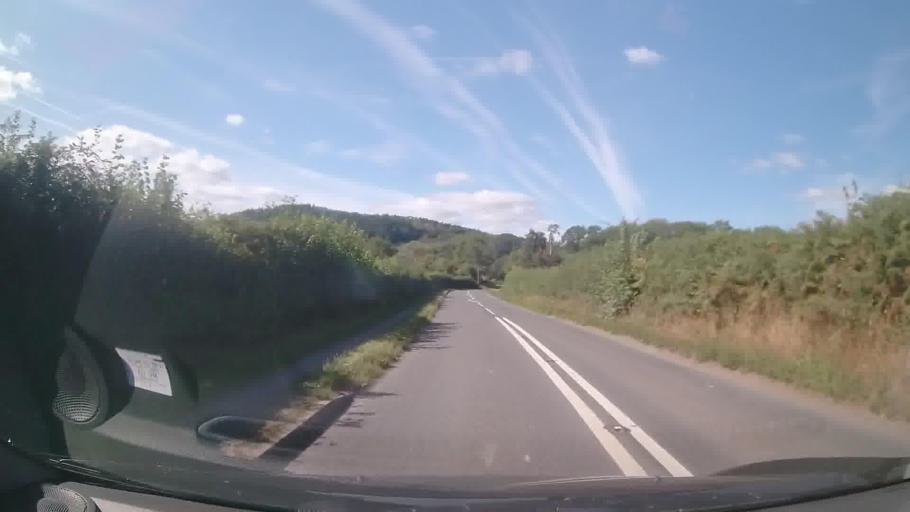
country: GB
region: Wales
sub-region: Sir Powys
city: Hay
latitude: 52.0833
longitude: -3.1433
